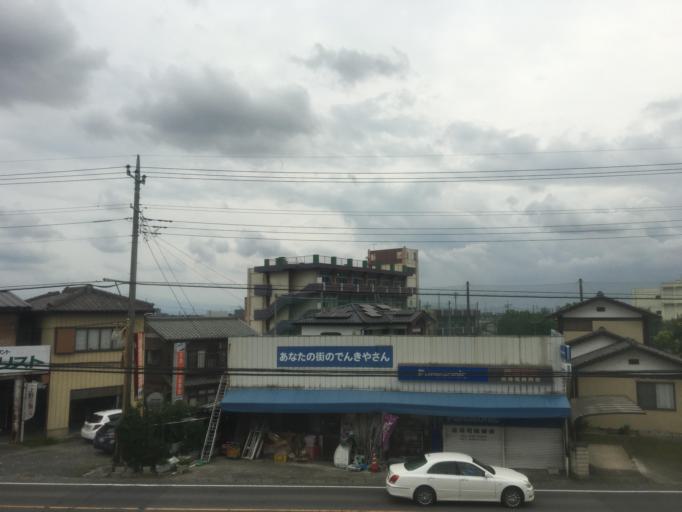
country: JP
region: Gunma
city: Fujioka
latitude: 36.2807
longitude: 139.0369
